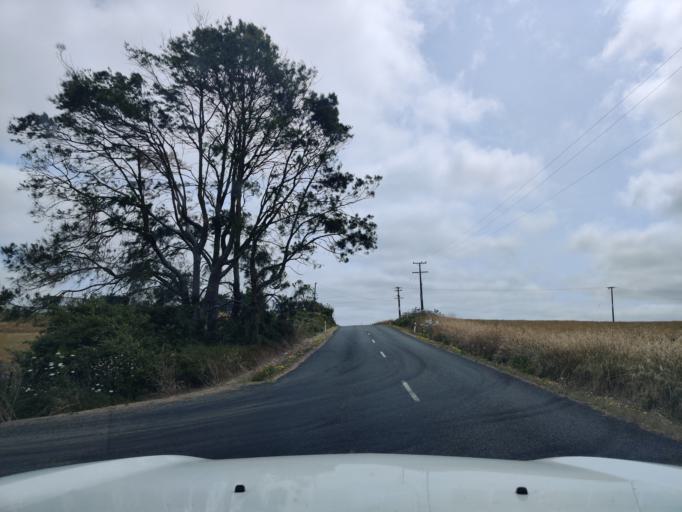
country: NZ
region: Waikato
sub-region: Waikato District
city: Te Kauwhata
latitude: -37.5108
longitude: 175.1783
